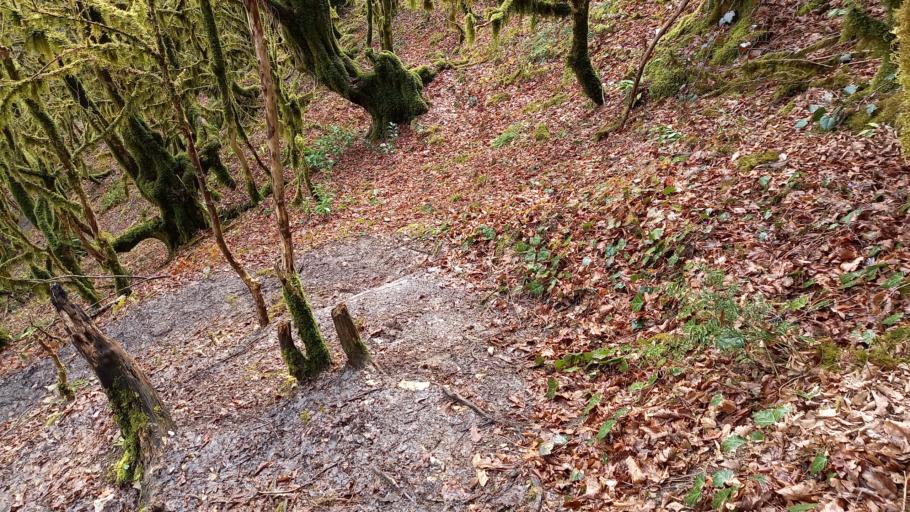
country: GE
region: Abkhazia
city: Dranda
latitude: 43.0291
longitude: 41.3321
